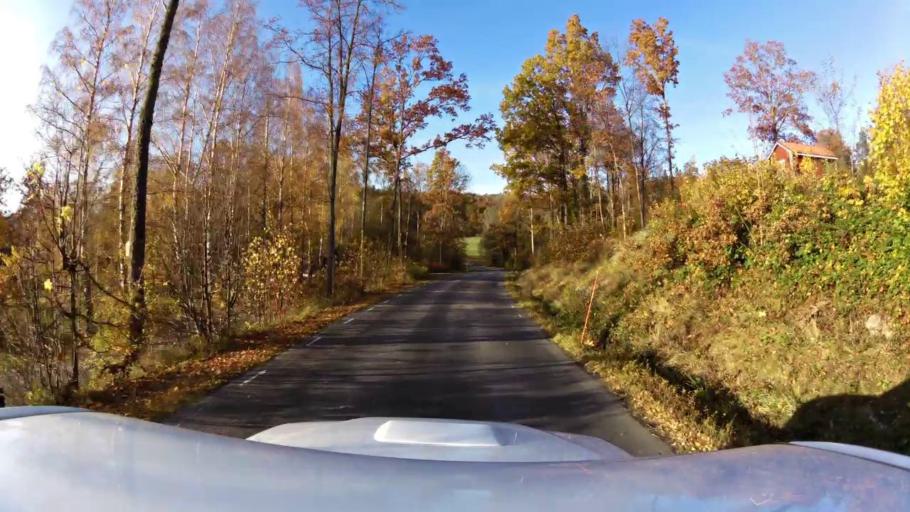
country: SE
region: OEstergoetland
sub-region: Kinda Kommun
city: Rimforsa
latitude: 58.1718
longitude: 15.6884
